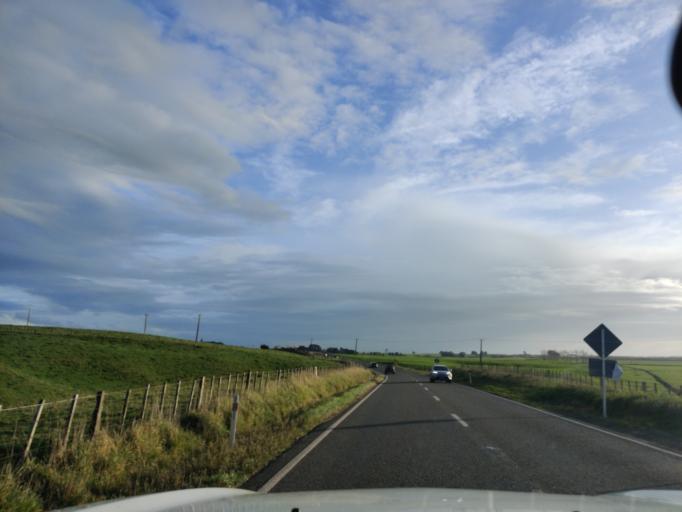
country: NZ
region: Manawatu-Wanganui
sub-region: Palmerston North City
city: Palmerston North
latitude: -40.4980
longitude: 175.4915
